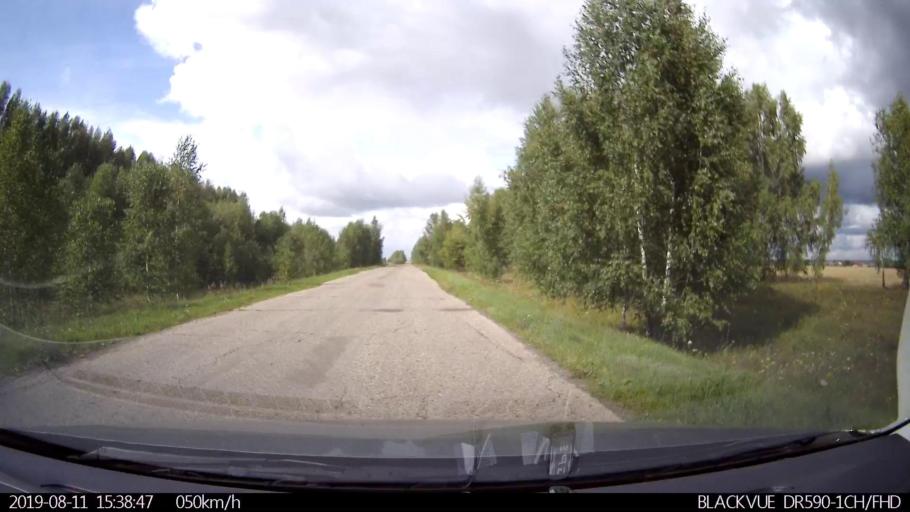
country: RU
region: Ulyanovsk
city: Ignatovka
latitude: 53.8638
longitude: 47.6401
